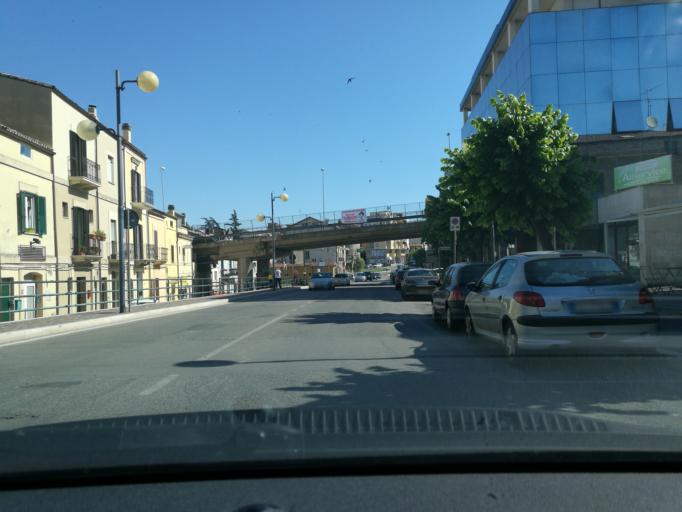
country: IT
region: Abruzzo
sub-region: Provincia di Chieti
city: Vasto
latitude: 42.1169
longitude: 14.7088
